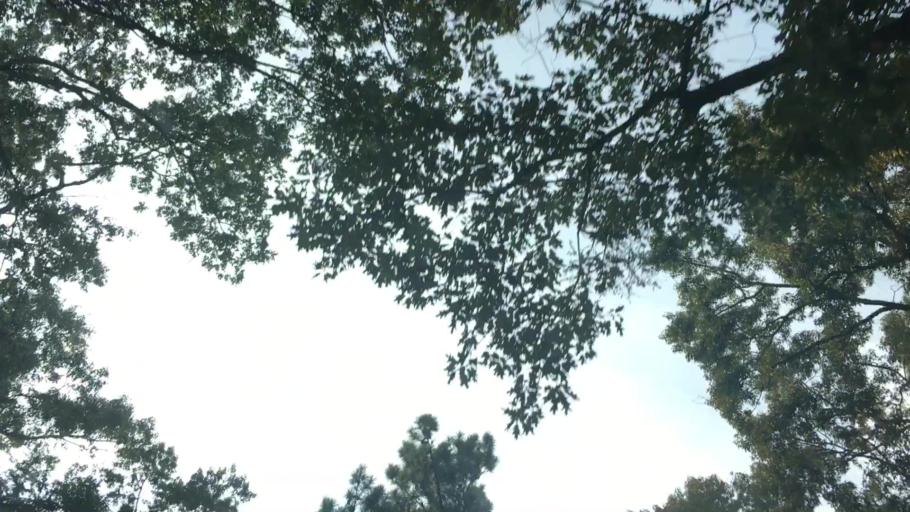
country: US
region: Alabama
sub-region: Bibb County
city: Woodstock
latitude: 33.2215
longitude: -87.1216
